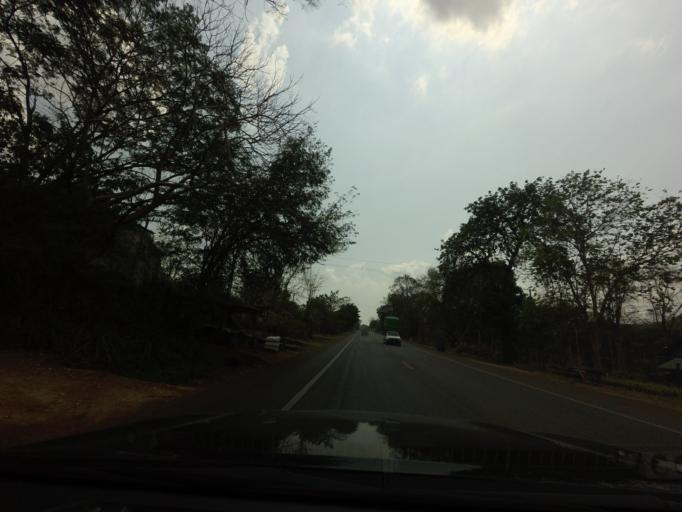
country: TH
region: Kanchanaburi
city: Sai Yok
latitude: 14.1449
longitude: 99.1459
